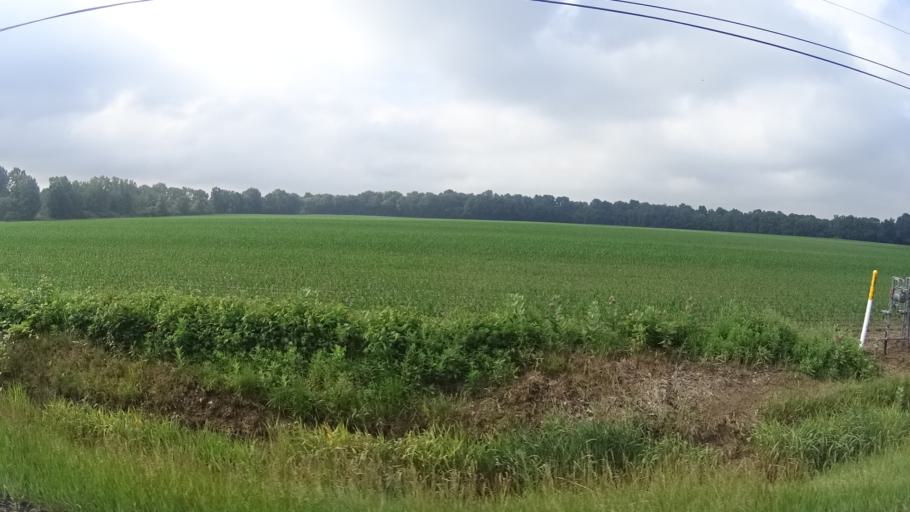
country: US
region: Ohio
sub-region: Erie County
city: Milan
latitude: 41.3038
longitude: -82.5073
